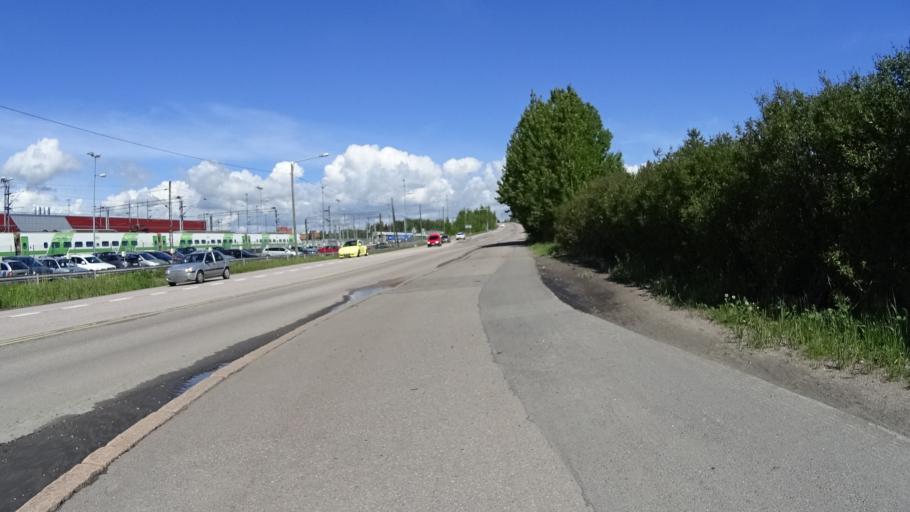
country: FI
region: Uusimaa
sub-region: Helsinki
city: Helsinki
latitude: 60.2126
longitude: 24.9320
